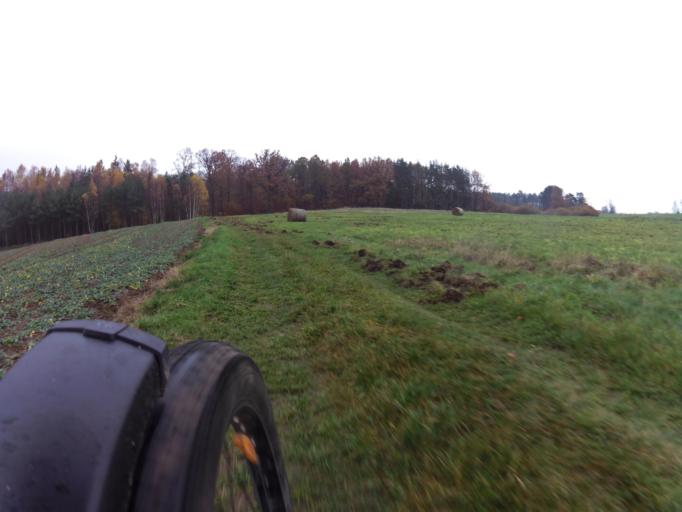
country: PL
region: Pomeranian Voivodeship
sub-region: Powiat pucki
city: Krokowa
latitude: 54.7295
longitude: 18.1320
